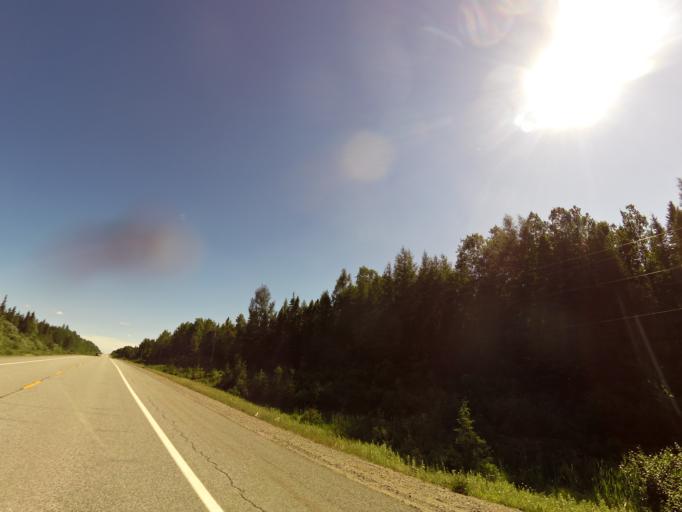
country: CA
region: Quebec
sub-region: Abitibi-Temiscamingue
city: Senneterre
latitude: 48.0171
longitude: -77.3606
